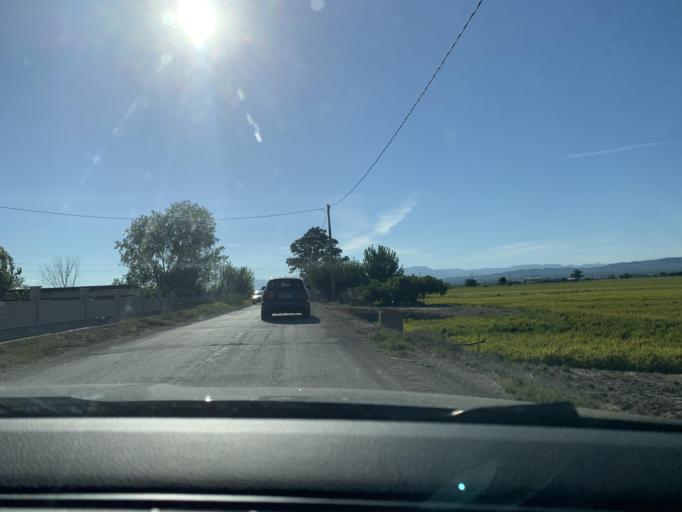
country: ES
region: Catalonia
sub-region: Provincia de Tarragona
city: Deltebre
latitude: 40.7480
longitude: 0.7309
